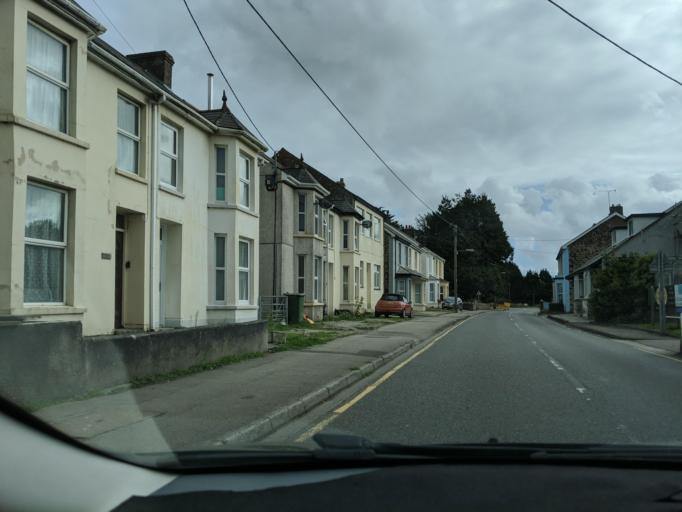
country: GB
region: England
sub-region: Cornwall
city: Par
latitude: 50.3585
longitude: -4.7131
